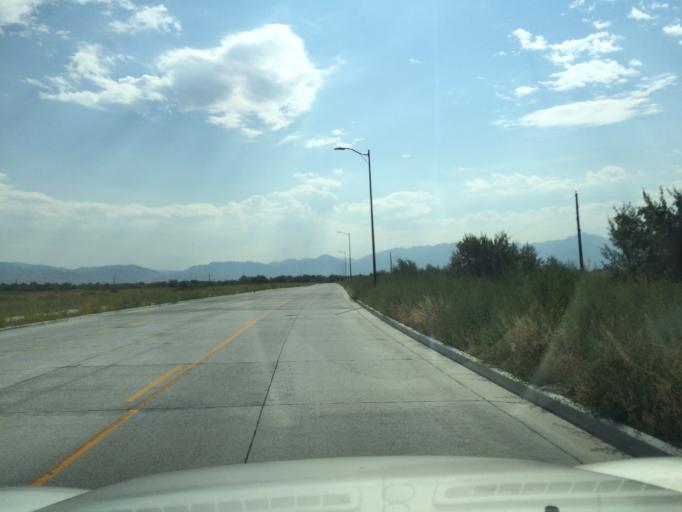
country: US
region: Utah
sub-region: Salt Lake County
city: Magna
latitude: 40.7150
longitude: -112.0502
